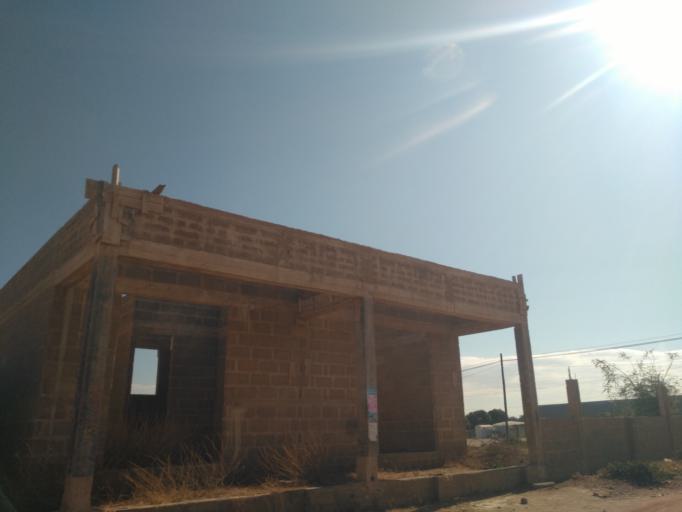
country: TZ
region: Dodoma
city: Dodoma
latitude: -6.1208
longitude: 35.7459
